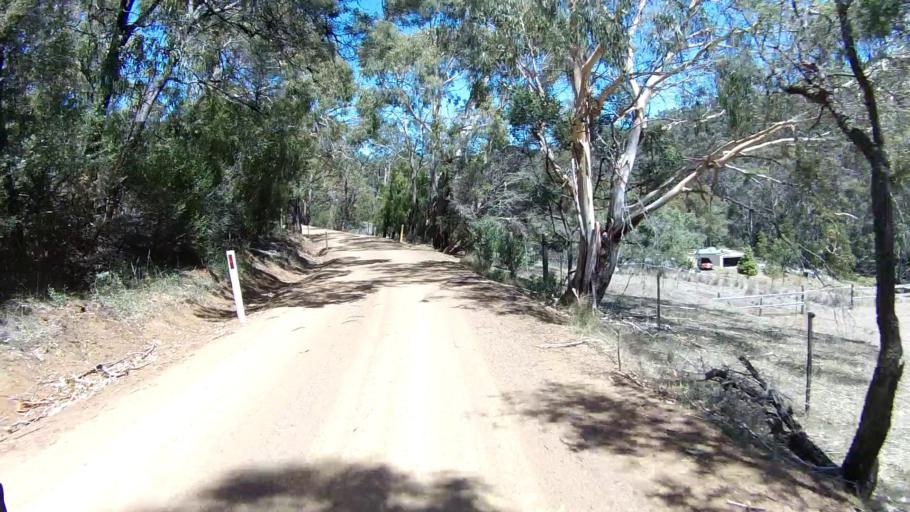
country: AU
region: Tasmania
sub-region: Clarence
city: Cambridge
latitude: -42.8502
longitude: 147.4390
